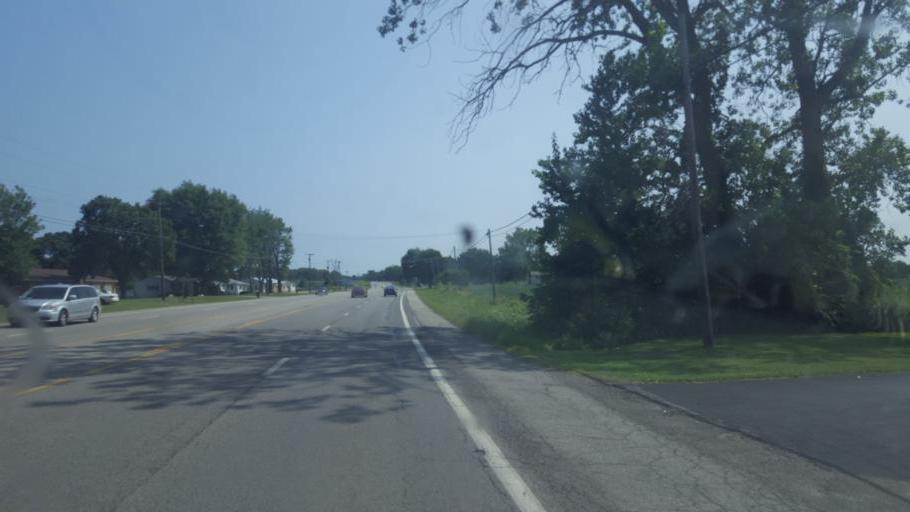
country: US
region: Ohio
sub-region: Richland County
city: Shelby
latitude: 40.8492
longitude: -82.6214
